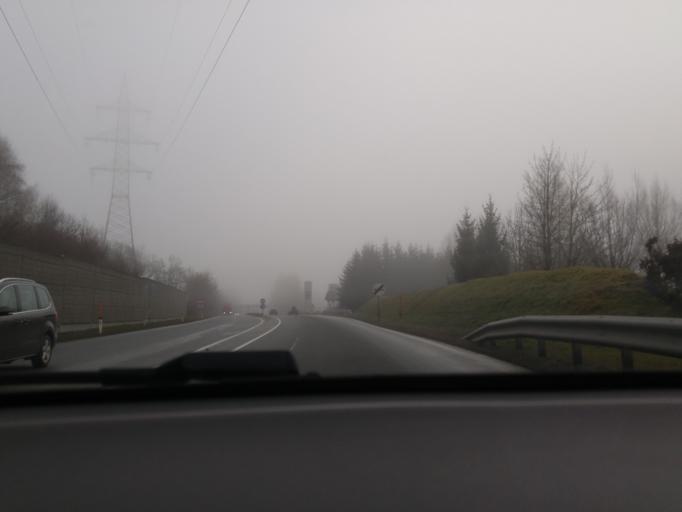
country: AT
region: Salzburg
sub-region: Politischer Bezirk Zell am See
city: Bruck an der Grossglocknerstrasse
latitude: 47.2815
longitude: 12.8154
